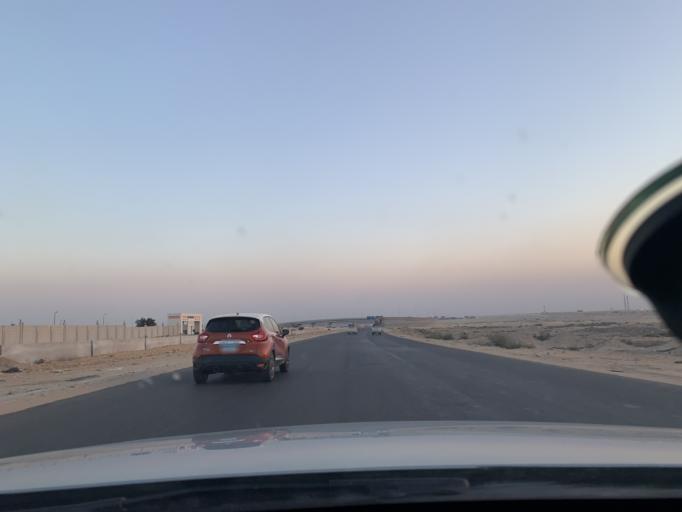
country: EG
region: Muhafazat al Qalyubiyah
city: Al Khankah
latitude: 30.2172
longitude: 31.4244
